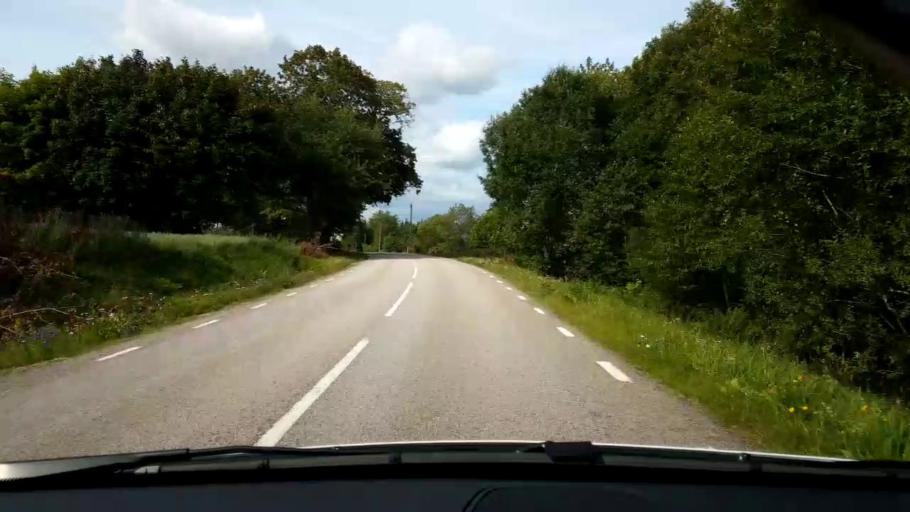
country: SE
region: Joenkoeping
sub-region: Vetlanda Kommun
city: Vetlanda
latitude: 57.3498
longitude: 15.0729
